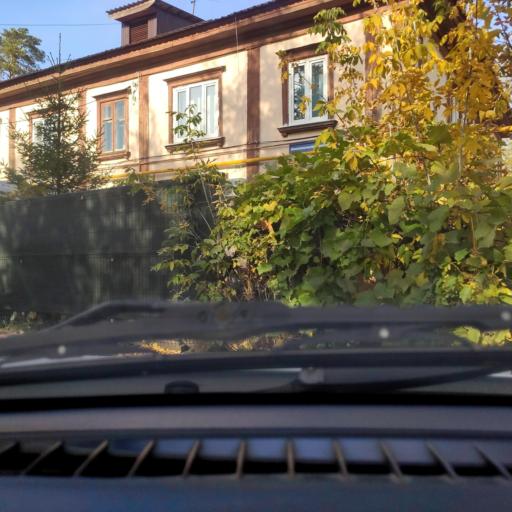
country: RU
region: Samara
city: Tol'yatti
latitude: 53.4759
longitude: 49.3698
